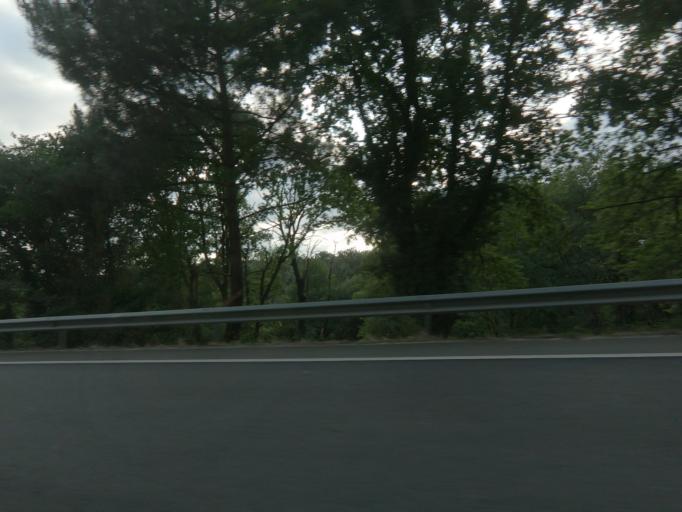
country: ES
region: Galicia
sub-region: Provincia de Ourense
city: Taboadela
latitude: 42.2552
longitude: -7.8347
